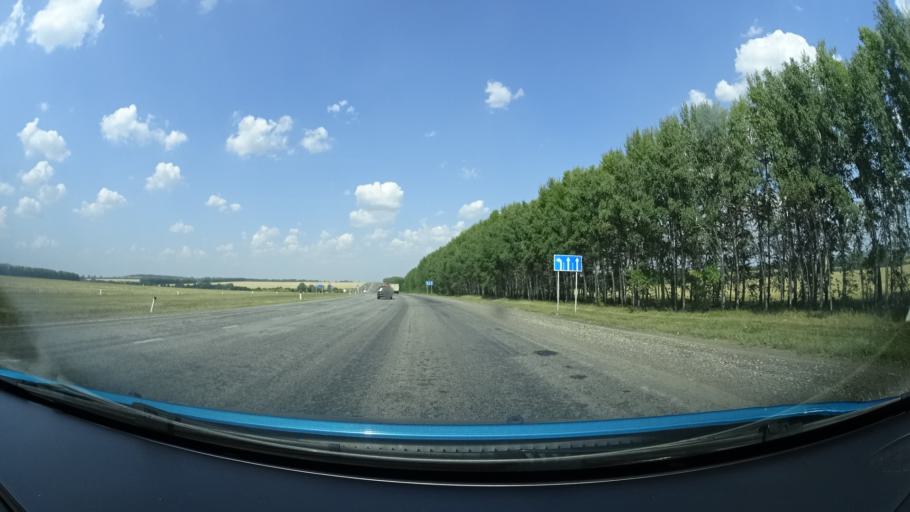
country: RU
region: Bashkortostan
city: Dmitriyevka
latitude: 54.6970
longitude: 55.2714
